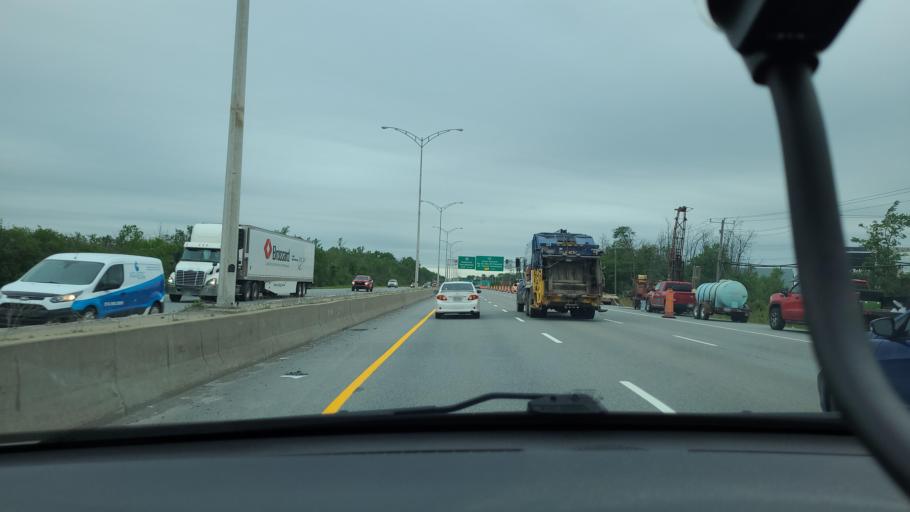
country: CA
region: Quebec
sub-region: Lanaudiere
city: Terrebonne
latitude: 45.6334
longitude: -73.6552
